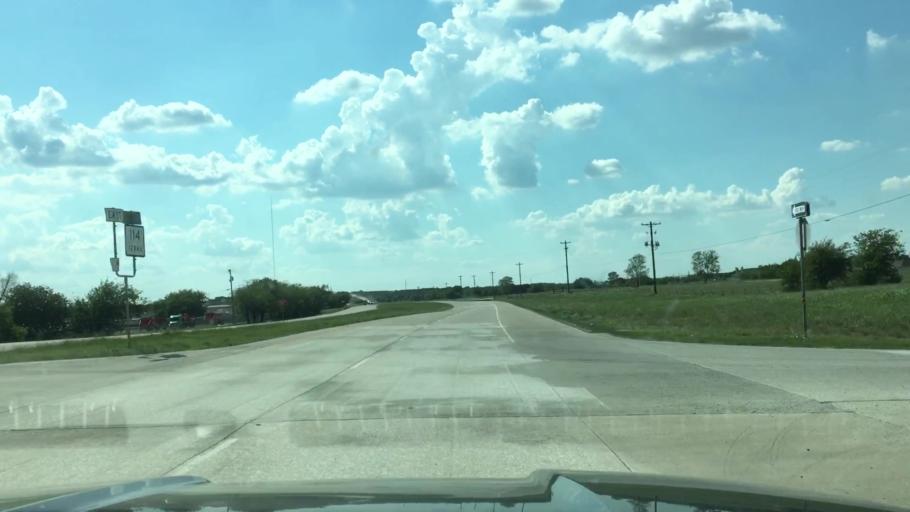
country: US
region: Texas
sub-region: Tarrant County
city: Haslet
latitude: 33.0363
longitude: -97.3916
